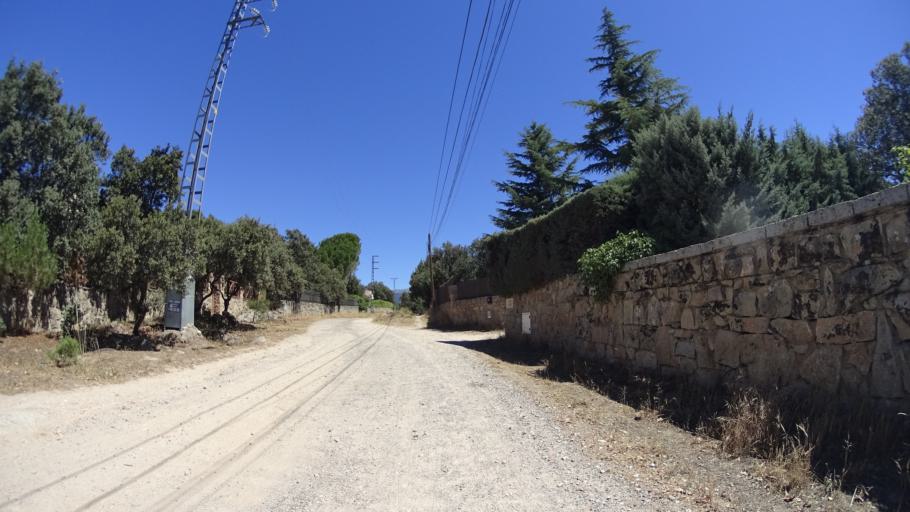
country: ES
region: Madrid
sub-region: Provincia de Madrid
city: Alpedrete
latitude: 40.6663
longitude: -4.0482
